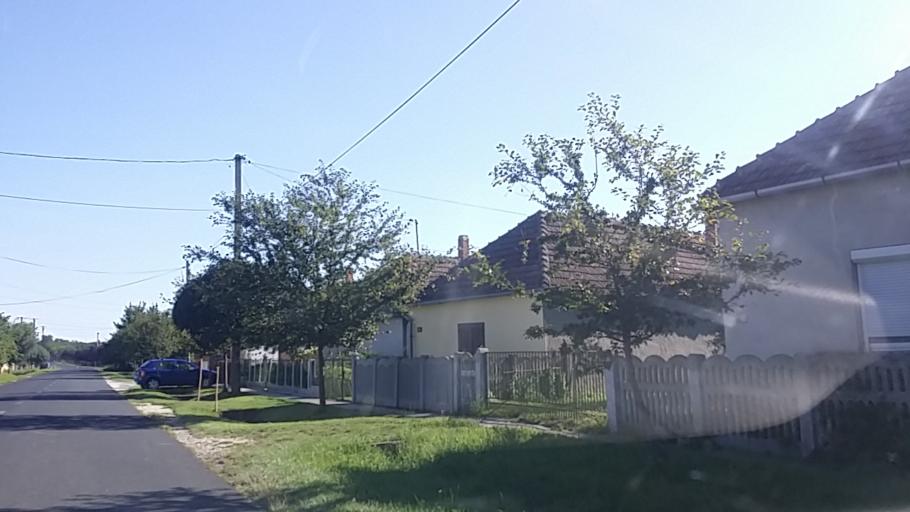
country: HU
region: Zala
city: Sarmellek
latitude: 46.6990
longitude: 17.1669
